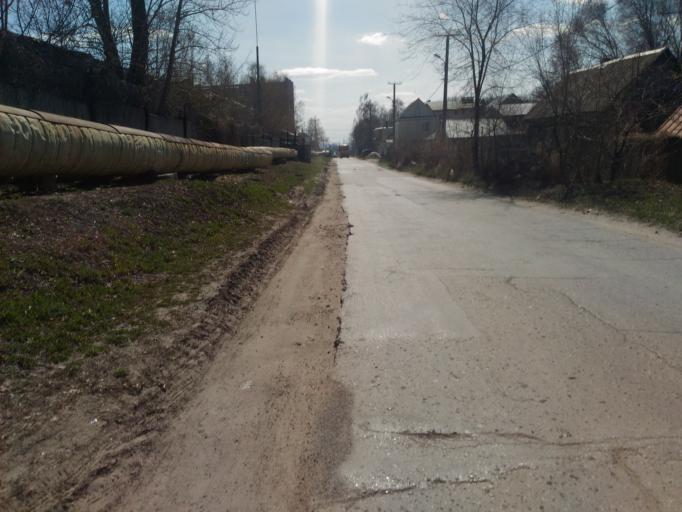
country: RU
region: Ulyanovsk
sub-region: Ulyanovskiy Rayon
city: Ulyanovsk
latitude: 54.3265
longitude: 48.3802
